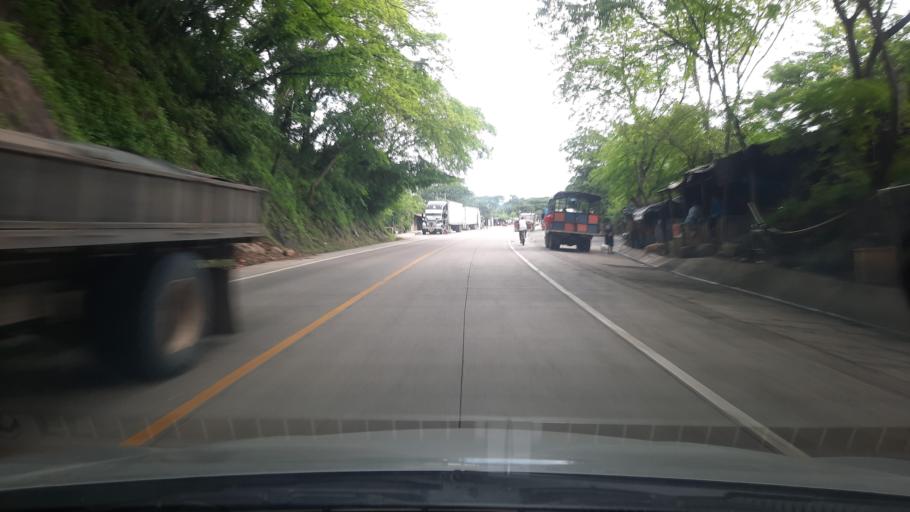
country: NI
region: Chinandega
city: Somotillo
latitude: 12.8632
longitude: -86.8521
